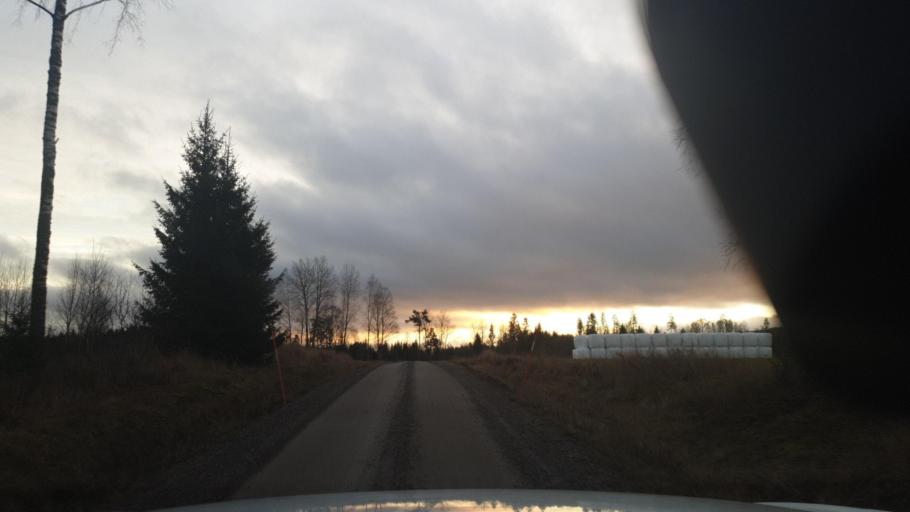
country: SE
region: Vaermland
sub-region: Eda Kommun
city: Charlottenberg
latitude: 59.7396
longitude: 12.1484
